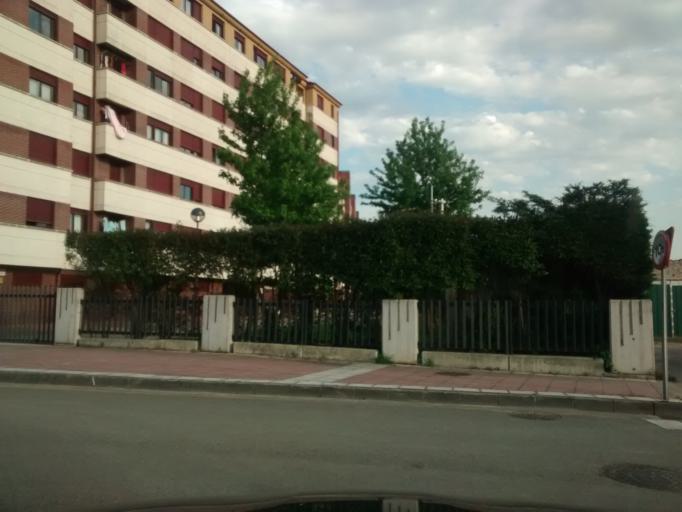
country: ES
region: Cantabria
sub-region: Provincia de Cantabria
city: El Astillero
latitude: 43.4391
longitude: -3.8458
